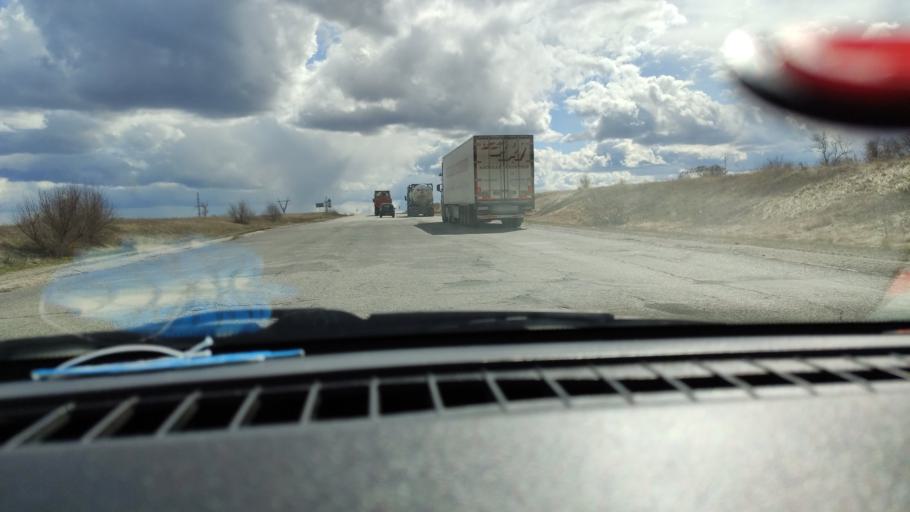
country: RU
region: Samara
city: Varlamovo
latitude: 53.0859
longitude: 48.3547
